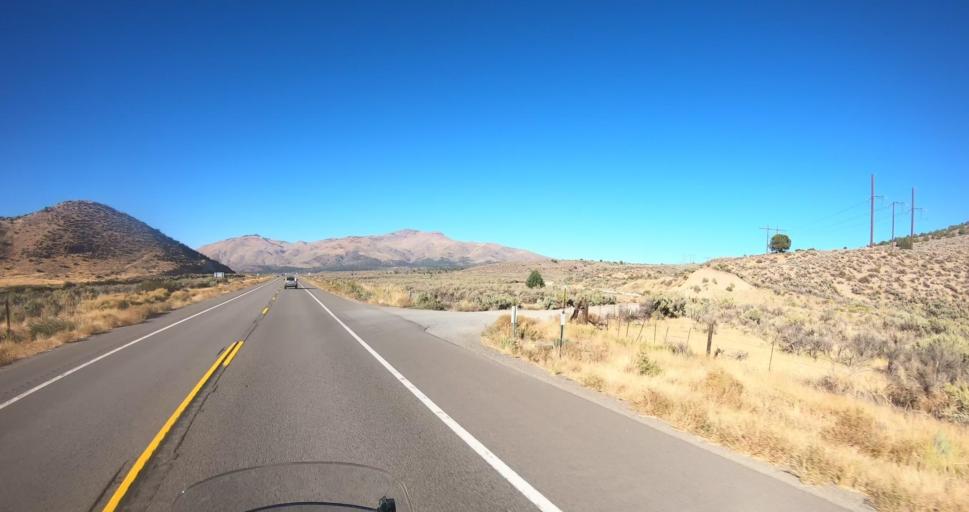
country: US
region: Nevada
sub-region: Washoe County
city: Cold Springs
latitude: 39.9258
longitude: -120.0185
